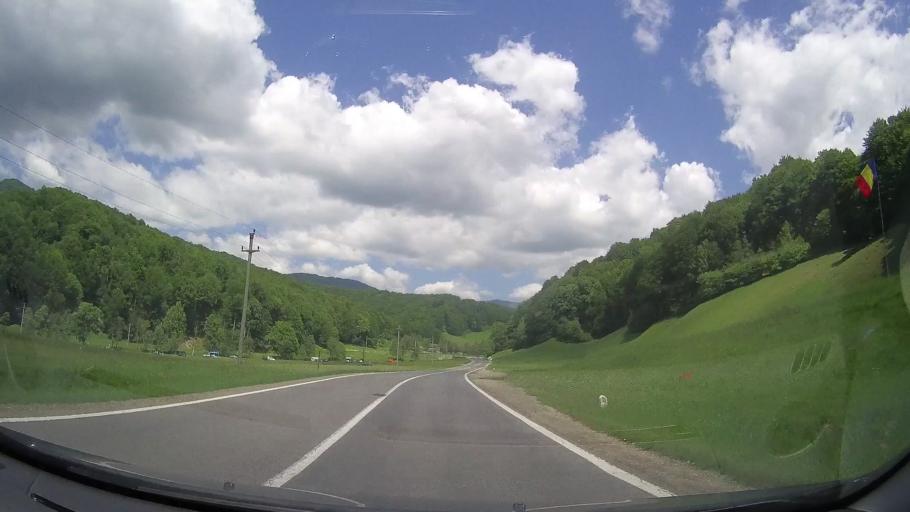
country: RO
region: Prahova
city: Maneciu
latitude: 45.4317
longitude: 25.9388
